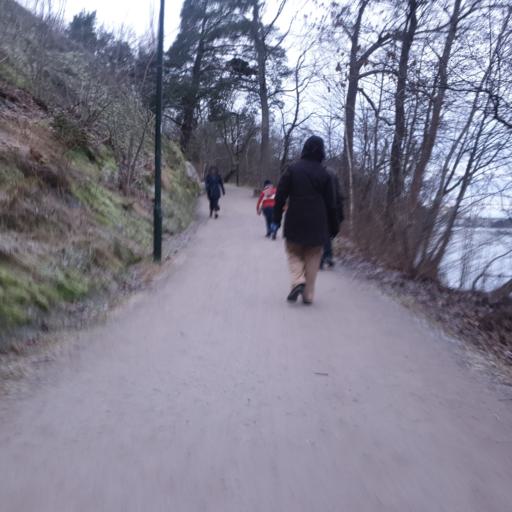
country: SE
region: Stockholm
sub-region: Stockholms Kommun
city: Arsta
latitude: 59.3022
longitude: 18.0692
